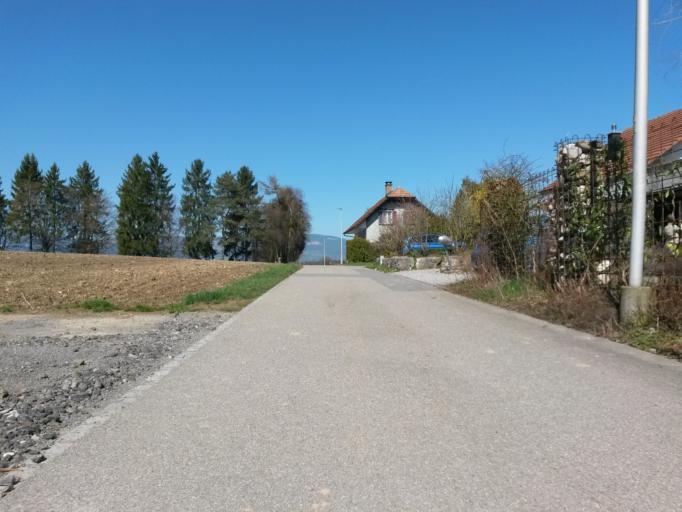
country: CH
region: Solothurn
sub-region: Bezirk Wasseramt
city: Kriegstetten
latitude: 47.1708
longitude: 7.6044
